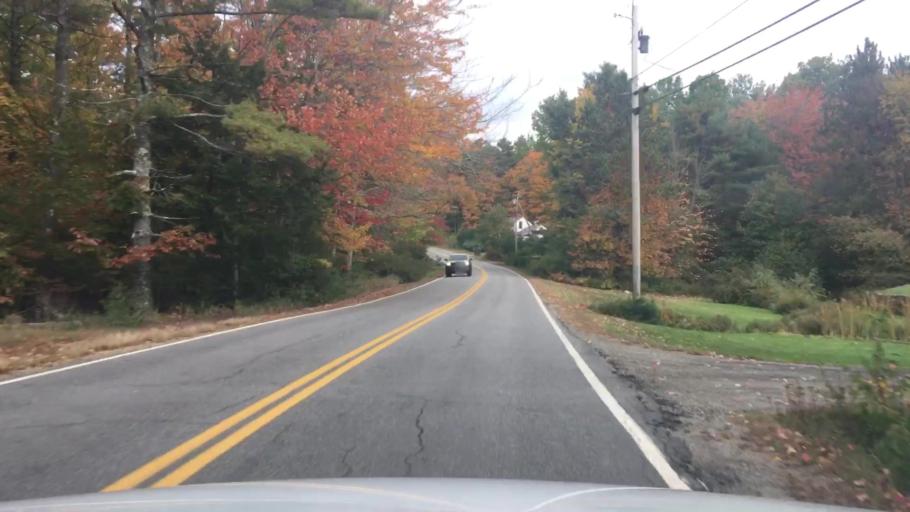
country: US
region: Maine
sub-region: Knox County
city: Hope
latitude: 44.2633
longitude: -69.1344
